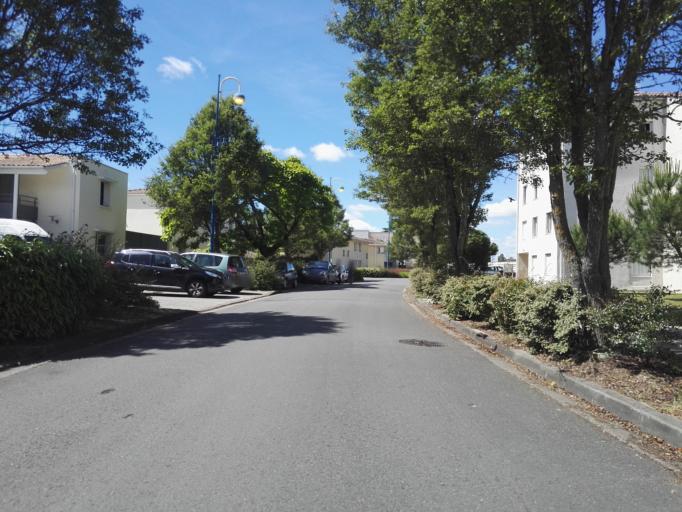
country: FR
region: Aquitaine
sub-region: Departement de la Gironde
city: Begles
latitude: 44.8010
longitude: -0.5400
